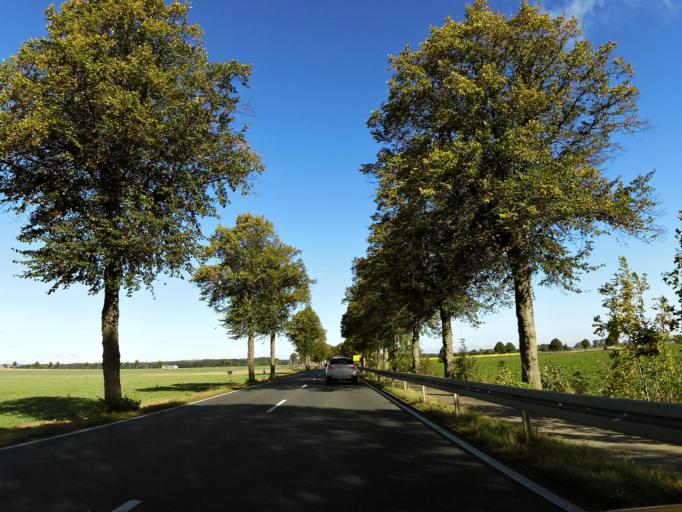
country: DE
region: Lower Saxony
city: Nordstemmen
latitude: 52.2046
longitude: 9.7475
